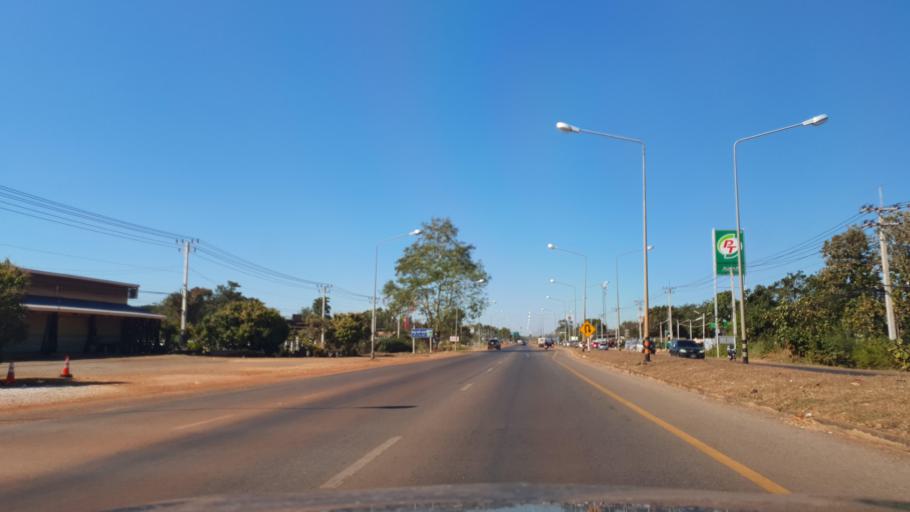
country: TH
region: Sakon Nakhon
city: Sakon Nakhon
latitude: 17.2632
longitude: 104.1406
